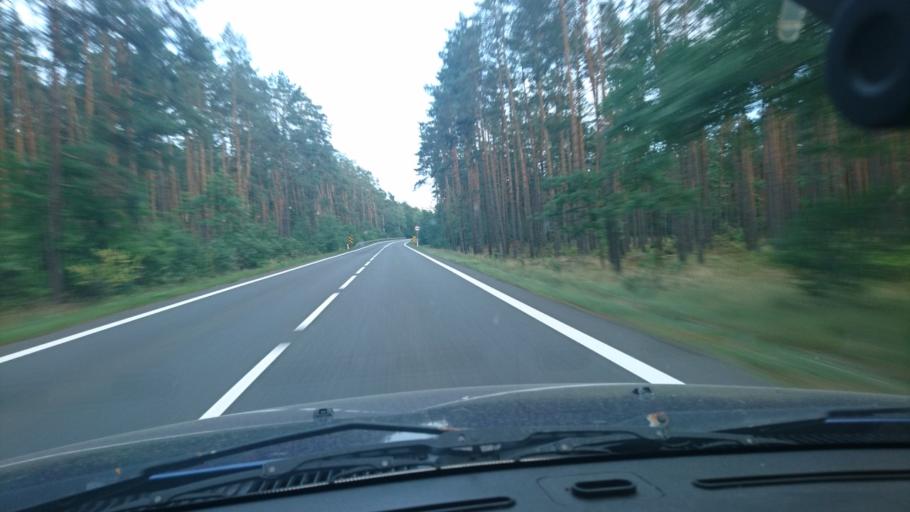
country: PL
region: Silesian Voivodeship
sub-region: Powiat lubliniecki
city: Lubliniec
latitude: 50.6034
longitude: 18.6999
